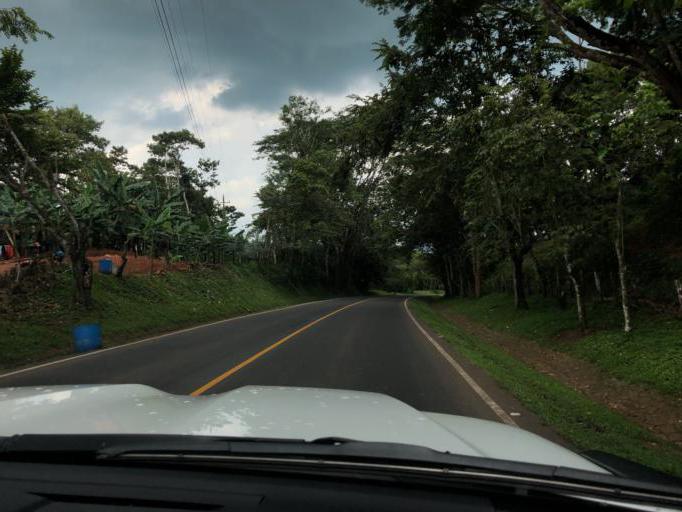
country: NI
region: Chontales
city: Villa Sandino
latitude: 11.9950
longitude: -84.8290
